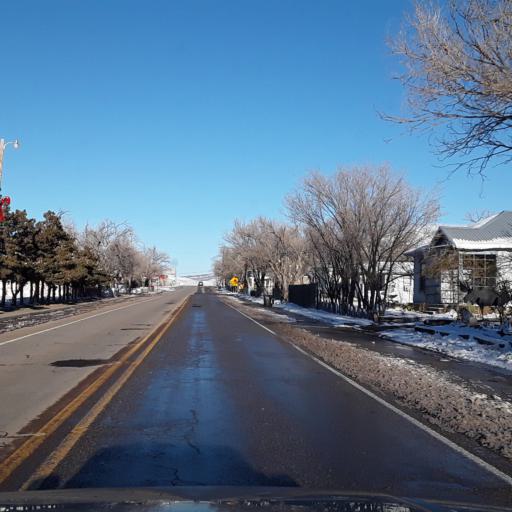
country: US
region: New Mexico
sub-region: Lincoln County
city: Carrizozo
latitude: 33.6441
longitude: -105.8744
